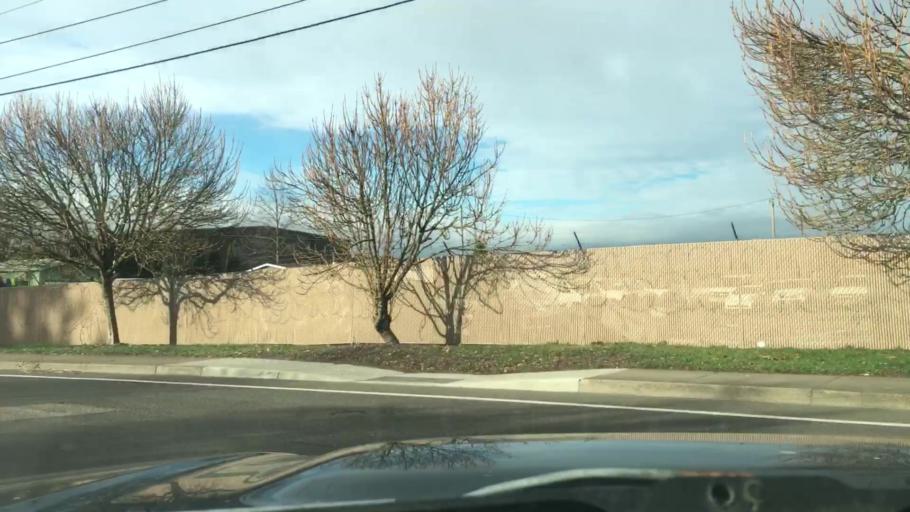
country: US
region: Oregon
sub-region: Lane County
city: Eugene
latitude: 44.0633
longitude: -123.1227
